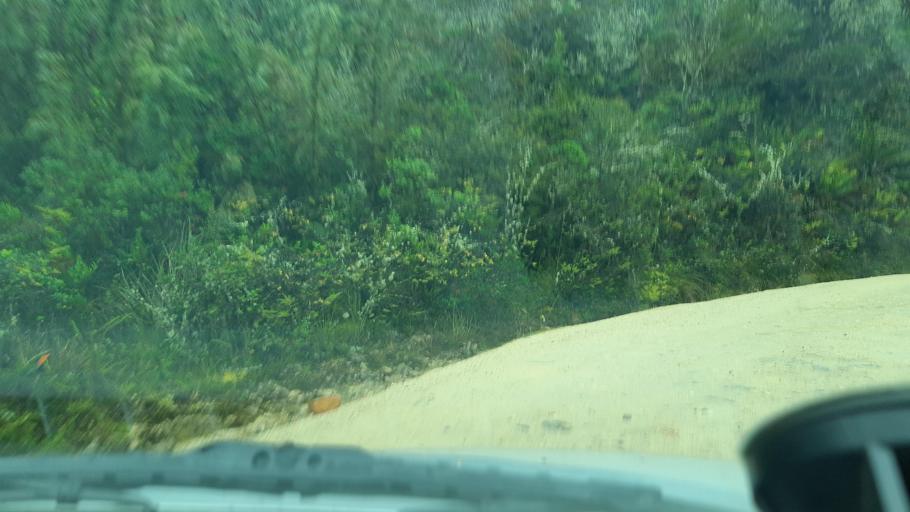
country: CO
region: Cundinamarca
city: Villapinzon
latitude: 5.2162
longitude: -73.5387
